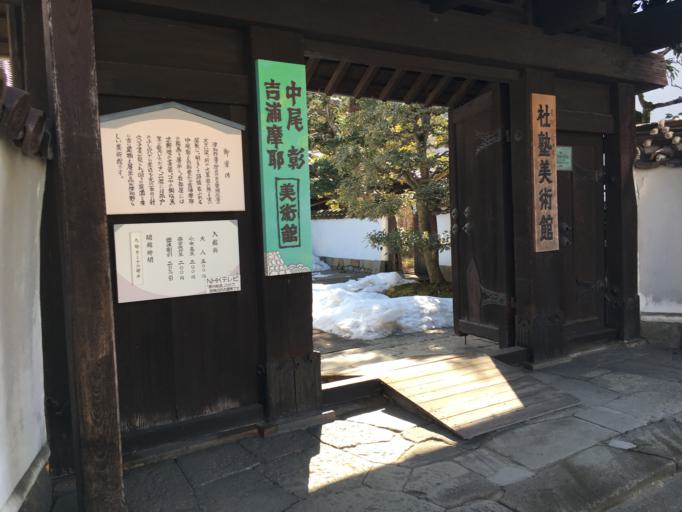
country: JP
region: Shimane
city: Masuda
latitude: 34.4646
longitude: 131.7730
